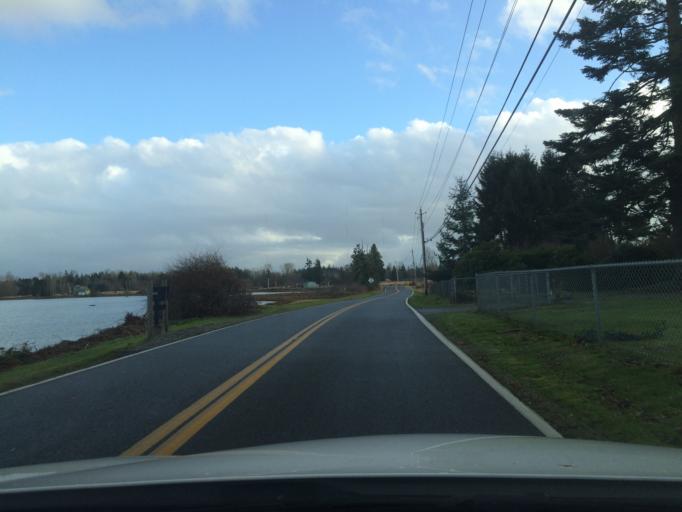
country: US
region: Washington
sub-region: Whatcom County
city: Blaine
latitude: 48.9592
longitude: -122.7528
